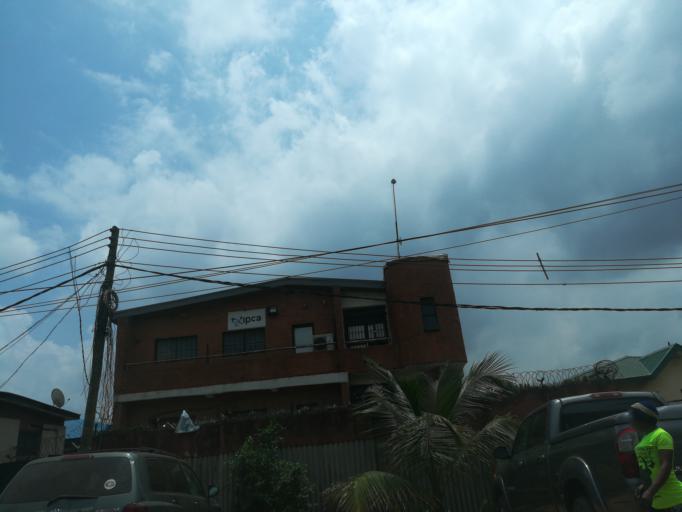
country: NG
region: Lagos
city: Oshodi
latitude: 6.5478
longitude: 3.3323
